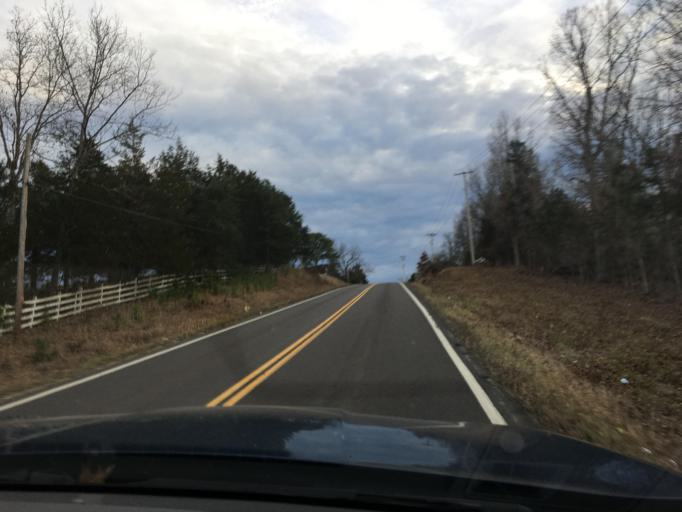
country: US
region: Missouri
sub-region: Jefferson County
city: De Soto
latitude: 38.0930
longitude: -90.5617
